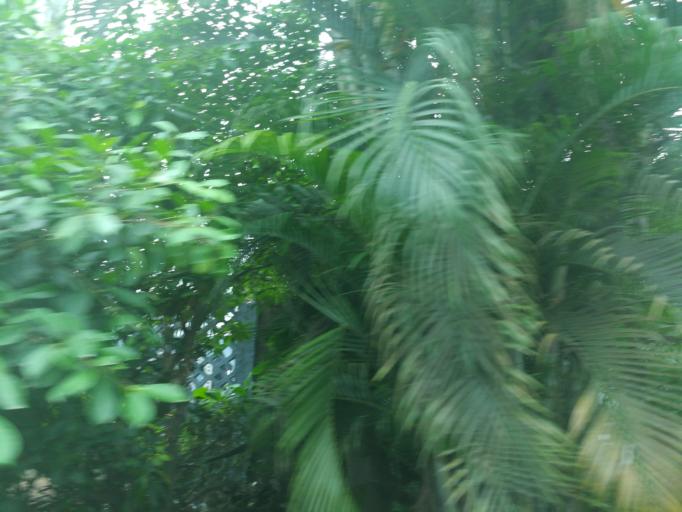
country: NG
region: Lagos
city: Ikoyi
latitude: 6.4345
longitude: 3.4165
